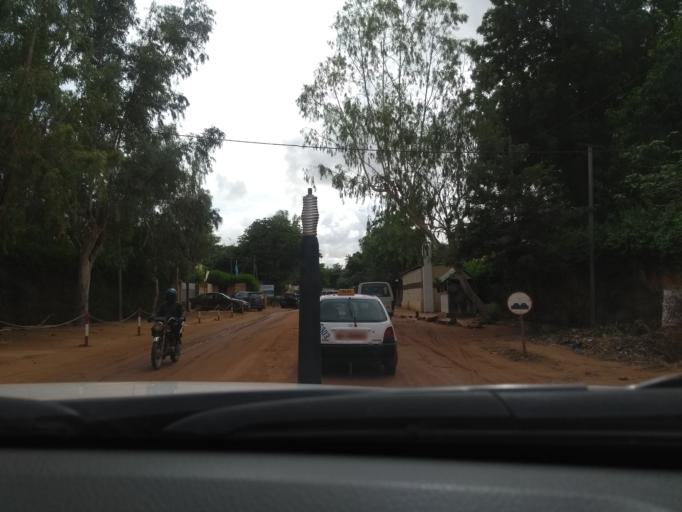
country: NE
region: Niamey
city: Niamey
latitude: 13.5222
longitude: 2.0936
